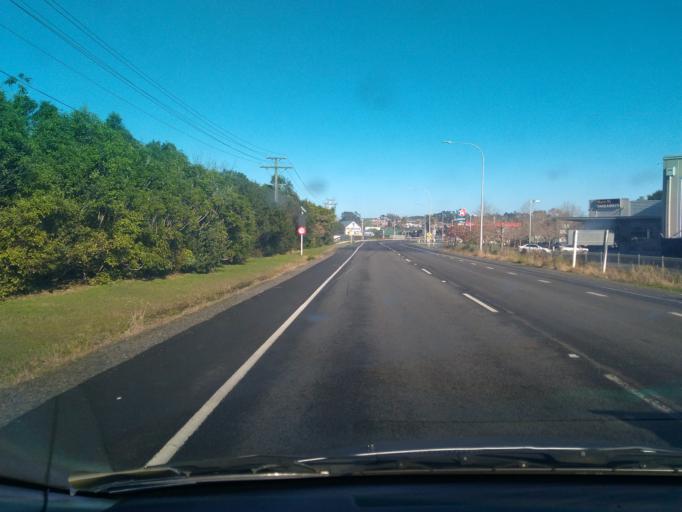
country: NZ
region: Auckland
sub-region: Auckland
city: Muriwai Beach
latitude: -36.7682
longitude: 174.4944
